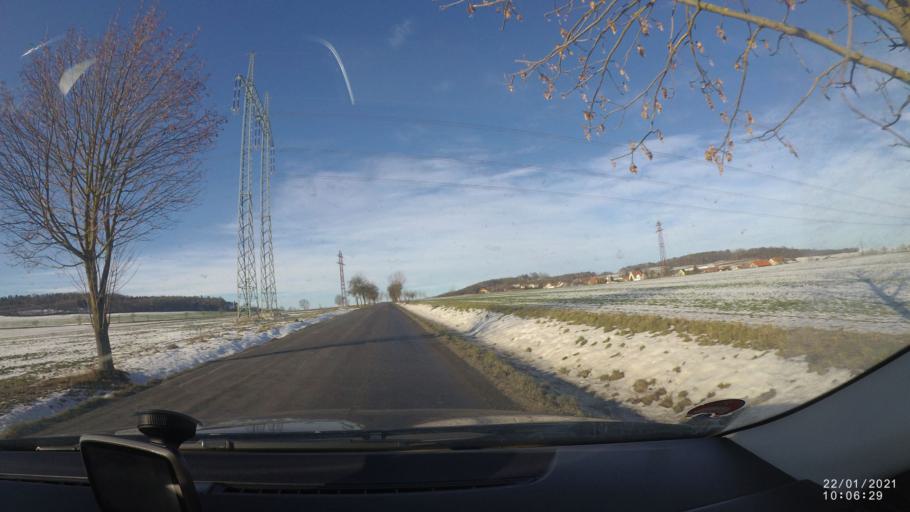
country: CZ
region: Central Bohemia
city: Chynava
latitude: 50.0066
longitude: 14.0980
